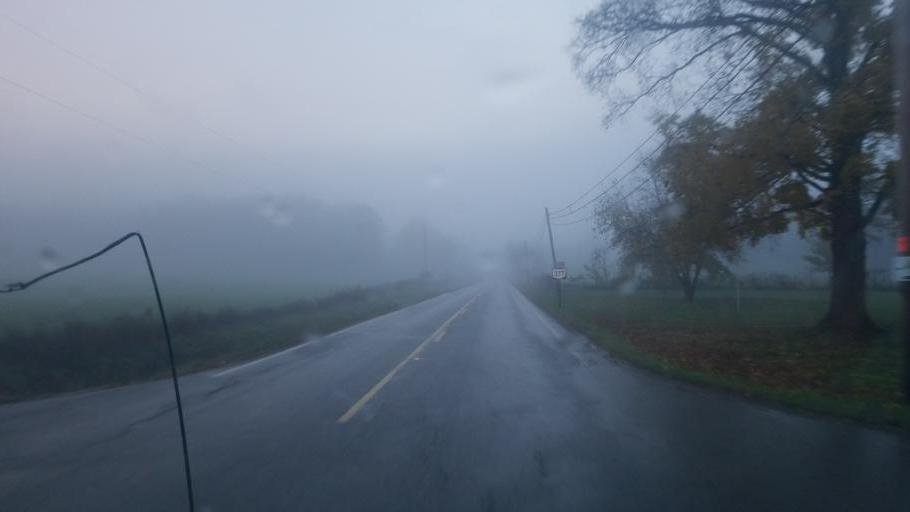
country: US
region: Ohio
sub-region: Morgan County
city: McConnelsville
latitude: 39.5059
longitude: -81.8563
